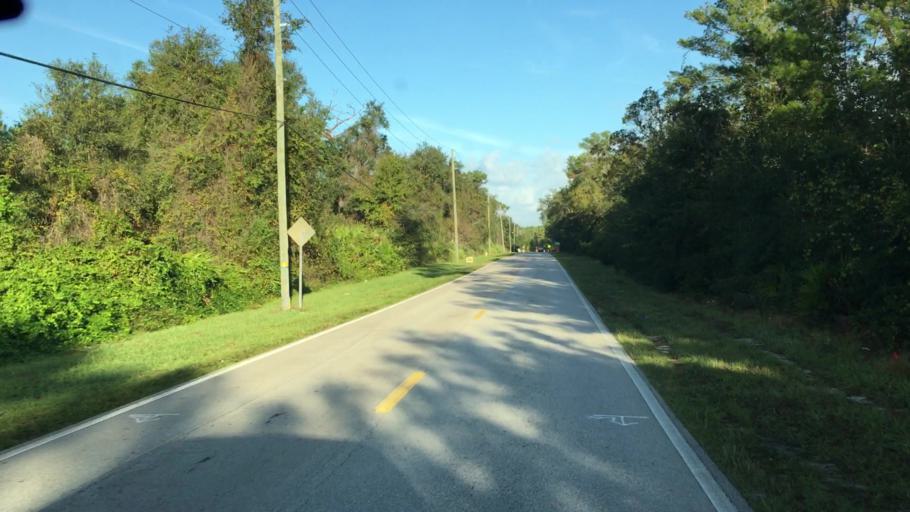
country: US
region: Florida
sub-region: Volusia County
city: North DeLand
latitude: 29.0632
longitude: -81.2679
